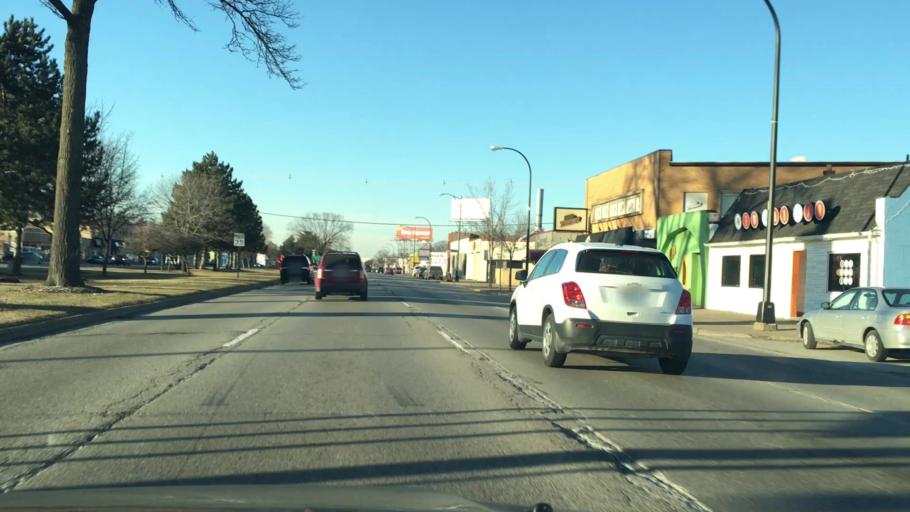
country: US
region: Michigan
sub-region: Oakland County
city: Ferndale
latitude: 42.4636
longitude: -83.1364
